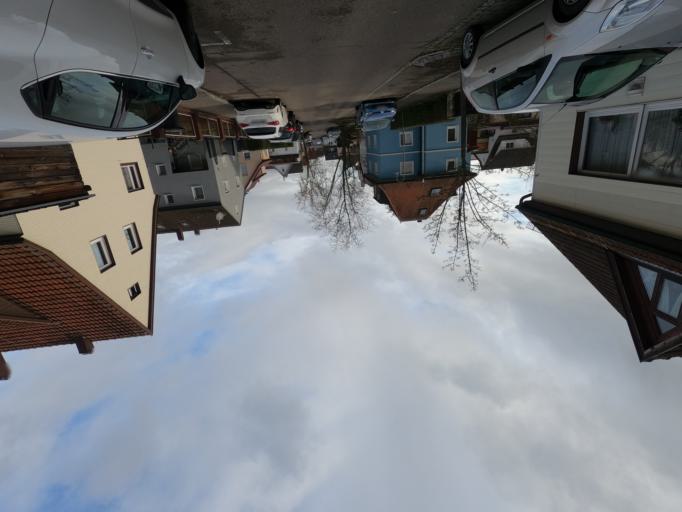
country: DE
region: Baden-Wuerttemberg
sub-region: Regierungsbezirk Stuttgart
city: Uhingen
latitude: 48.7060
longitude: 9.5939
